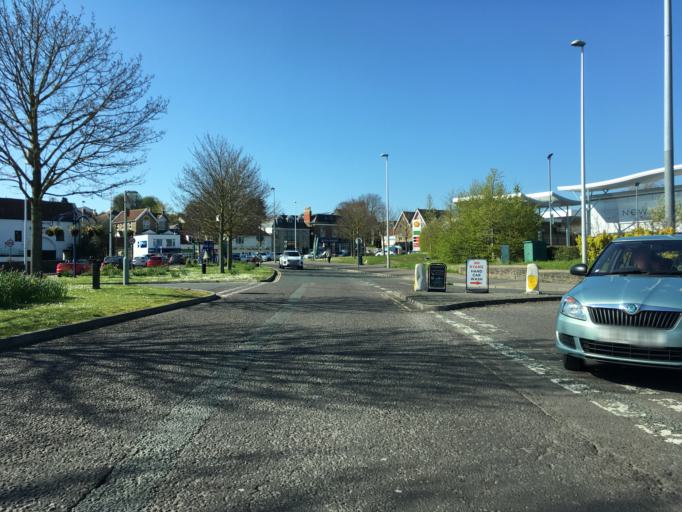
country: GB
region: England
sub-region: North Somerset
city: Portishead
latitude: 51.4847
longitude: -2.7671
